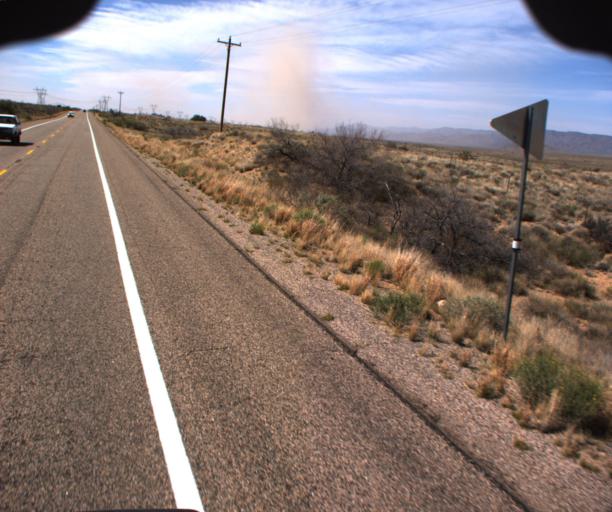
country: US
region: Arizona
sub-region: Mohave County
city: New Kingman-Butler
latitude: 35.3885
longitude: -113.7386
